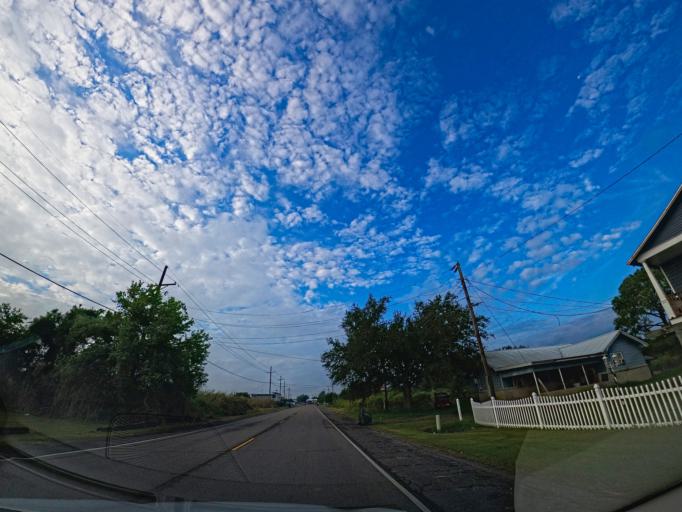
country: US
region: Louisiana
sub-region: Terrebonne Parish
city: Chauvin
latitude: 29.4109
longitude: -90.6066
